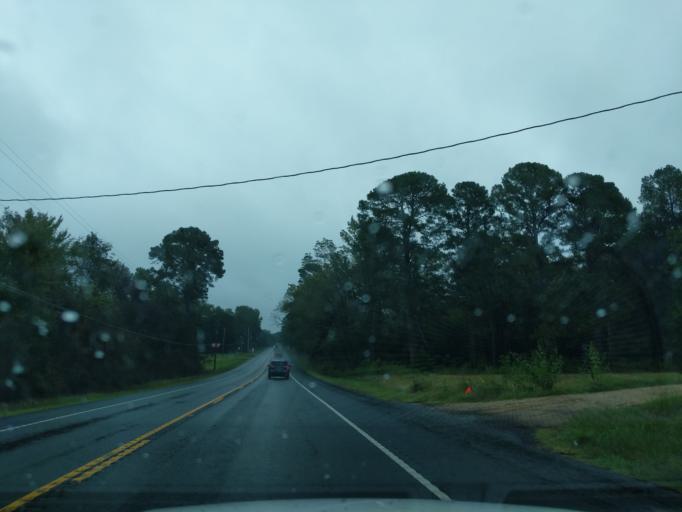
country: US
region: Louisiana
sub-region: Caddo Parish
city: Greenwood
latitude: 32.3759
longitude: -94.0324
